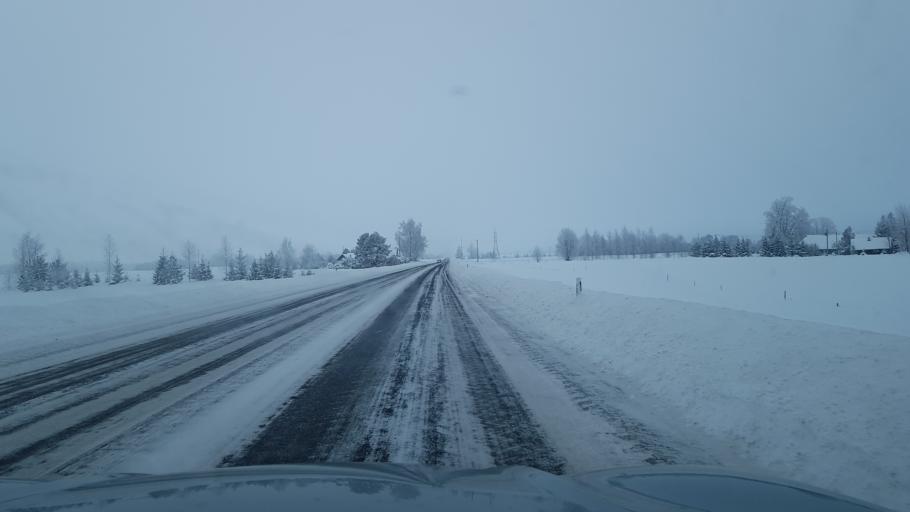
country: EE
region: Ida-Virumaa
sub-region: Johvi vald
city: Johvi
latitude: 59.2353
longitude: 27.3472
